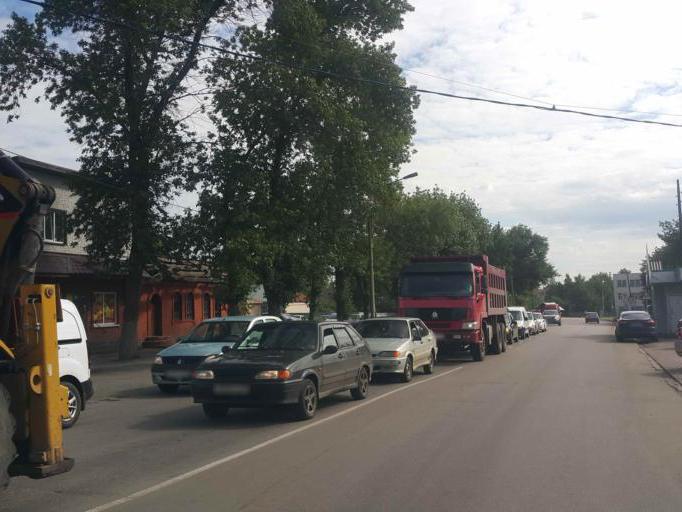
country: RU
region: Tambov
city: Pokrovo-Prigorodnoye
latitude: 52.7093
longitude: 41.4188
